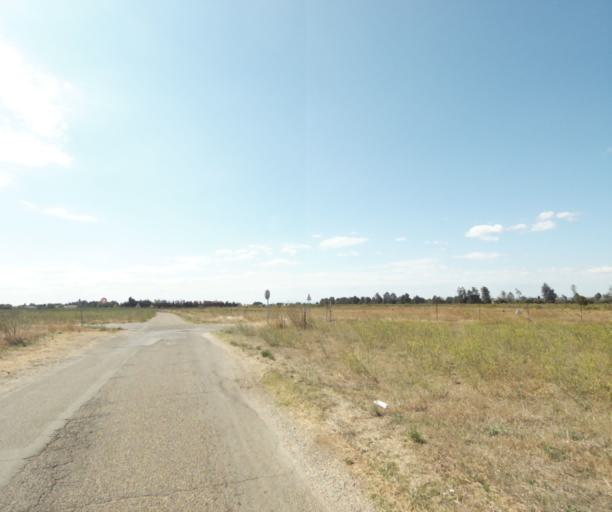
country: FR
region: Languedoc-Roussillon
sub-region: Departement du Gard
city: Bouillargues
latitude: 43.8001
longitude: 4.4478
